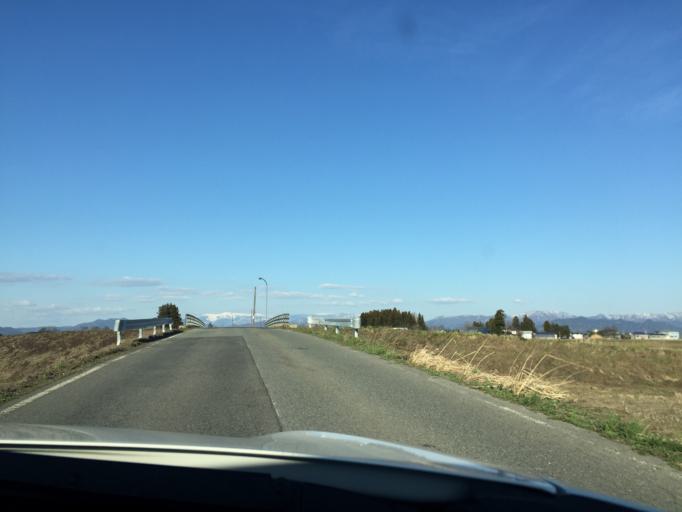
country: JP
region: Yamagata
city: Yonezawa
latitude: 37.9822
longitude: 140.0728
